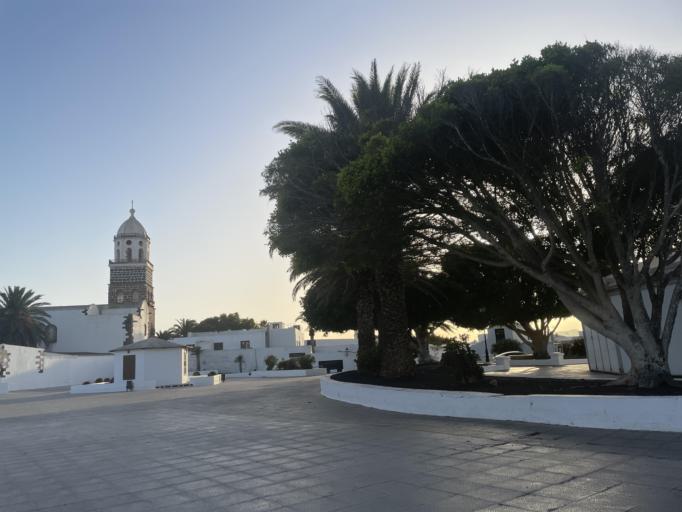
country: ES
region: Canary Islands
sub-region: Provincia de Las Palmas
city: Teguise
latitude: 29.0603
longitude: -13.5594
